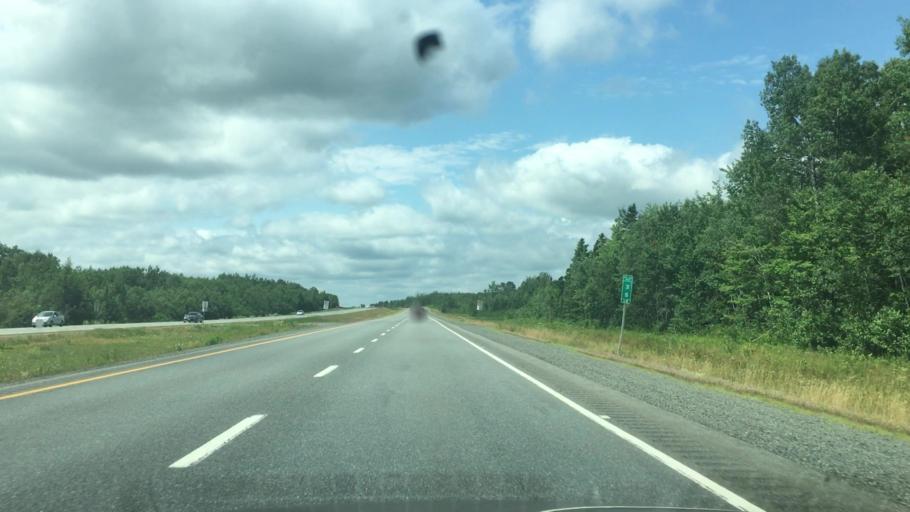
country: CA
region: Nova Scotia
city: Oxford
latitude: 45.7138
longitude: -63.9379
